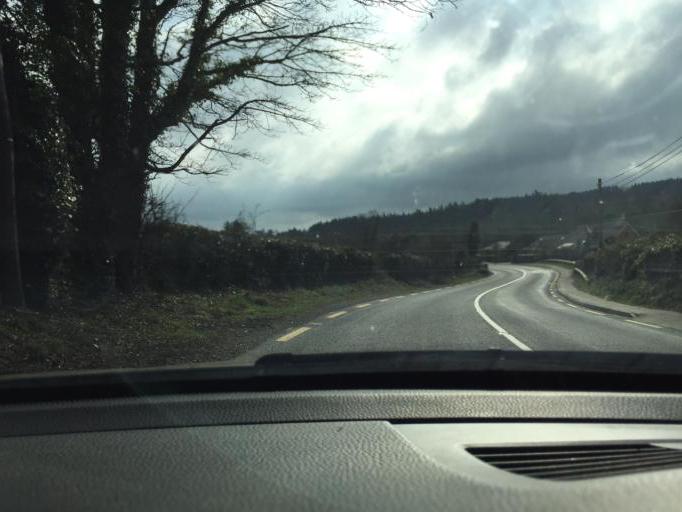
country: IE
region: Leinster
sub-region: South Dublin
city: Saggart
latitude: 53.2526
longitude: -6.4515
